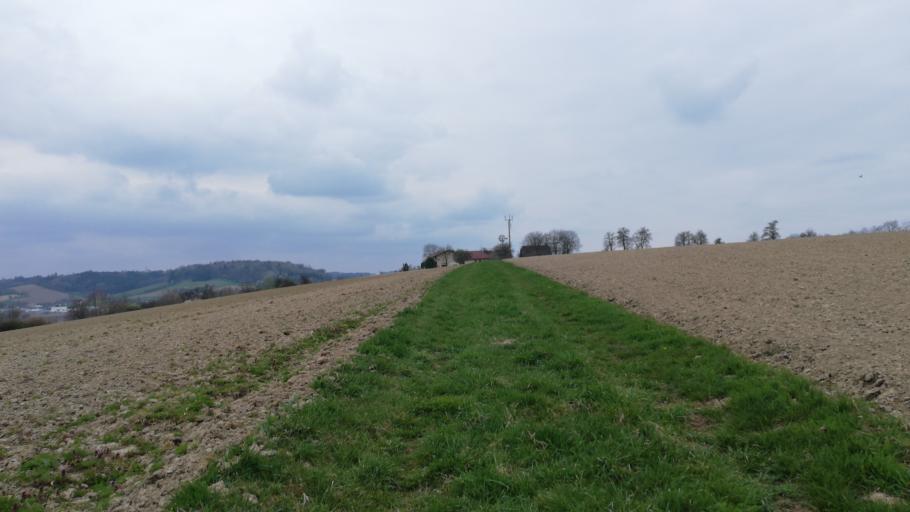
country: AT
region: Upper Austria
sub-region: Politischer Bezirk Grieskirchen
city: Bad Schallerbach
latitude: 48.2228
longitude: 13.9524
